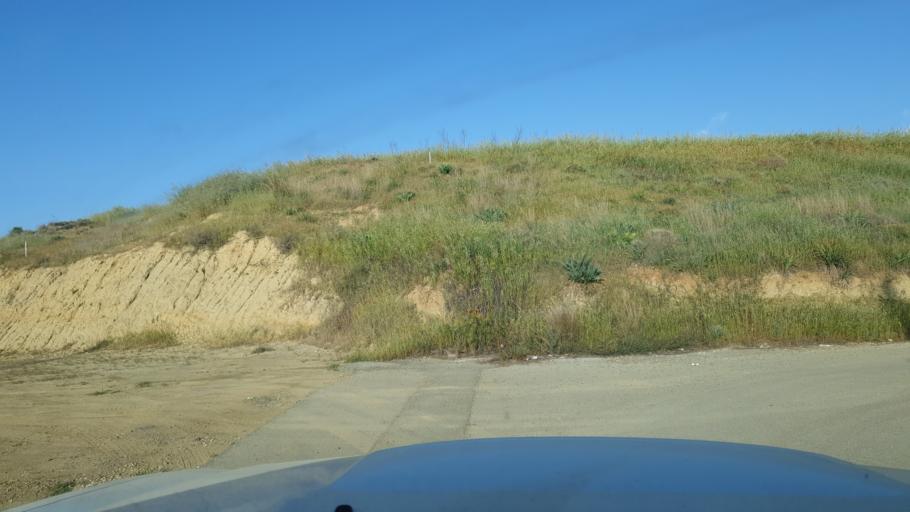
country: CY
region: Lefkosia
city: Tseri
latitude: 35.0599
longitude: 33.3272
